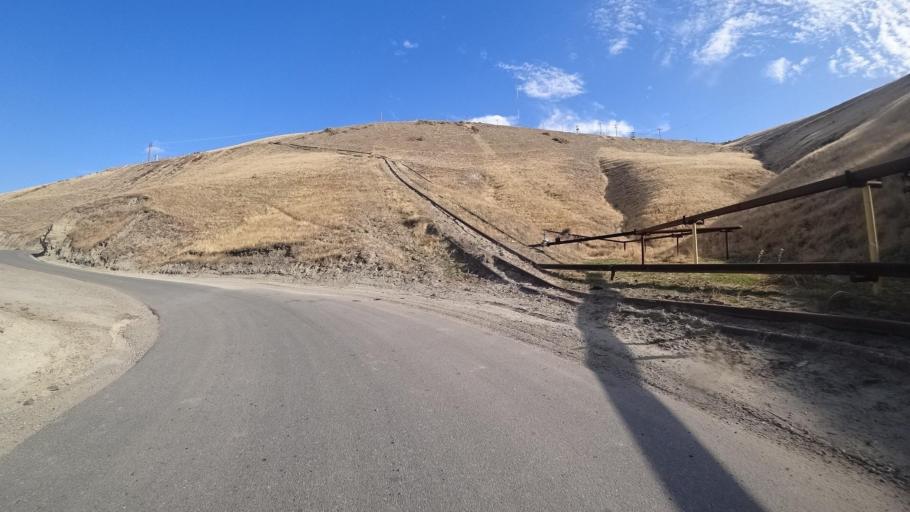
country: US
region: California
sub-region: Kern County
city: Oildale
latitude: 35.4878
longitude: -118.8930
